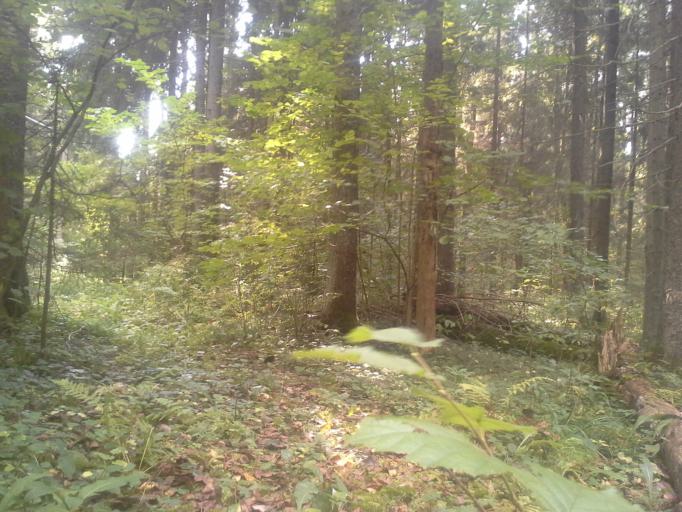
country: RU
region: Moskovskaya
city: Selyatino
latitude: 55.4607
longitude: 36.9849
